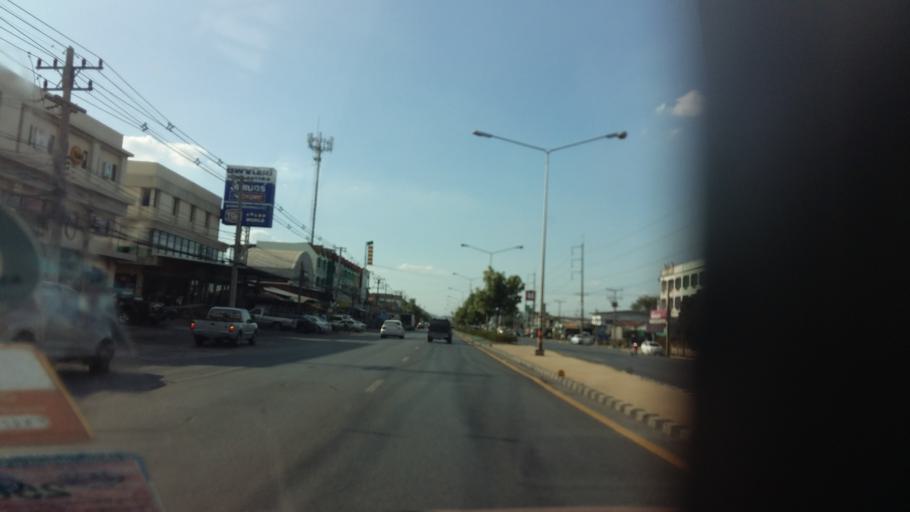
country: TH
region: Lop Buri
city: Lop Buri
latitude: 14.8206
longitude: 100.6483
